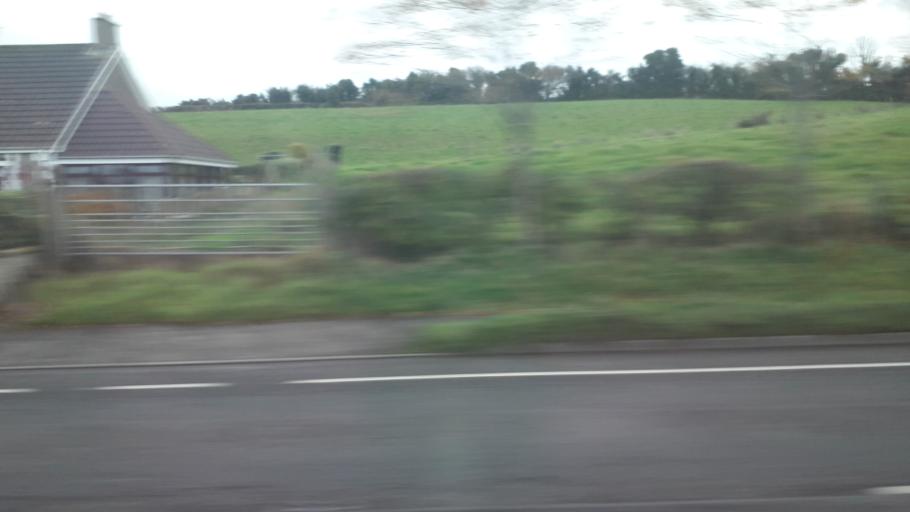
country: GB
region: Northern Ireland
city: Londonderry County Borough
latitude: 54.9364
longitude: -7.3920
